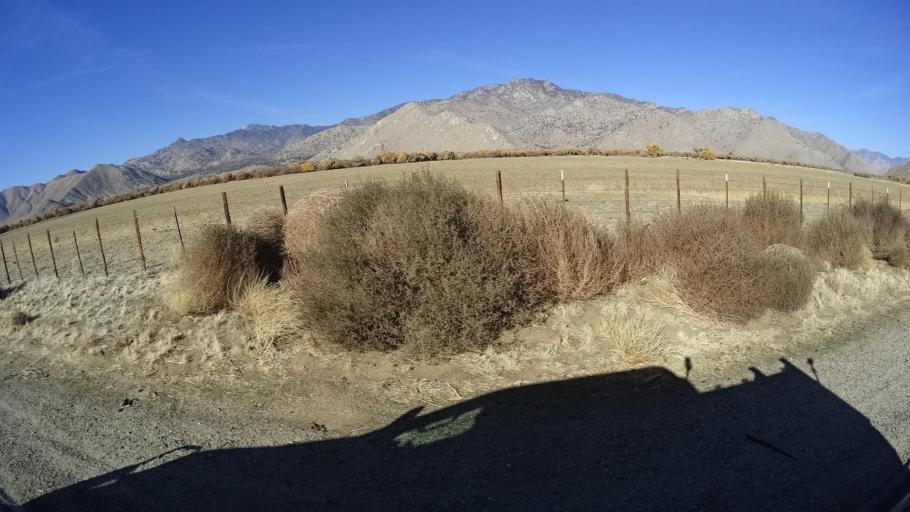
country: US
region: California
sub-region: Kern County
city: Weldon
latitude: 35.6670
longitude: -118.2754
